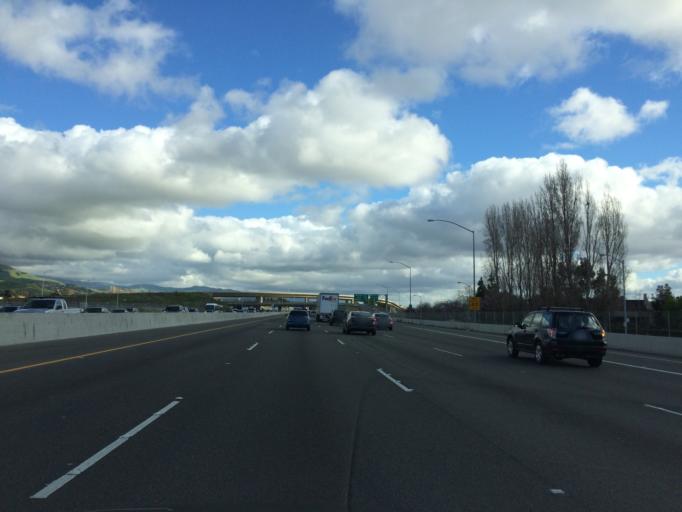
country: US
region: California
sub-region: Santa Clara County
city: Milpitas
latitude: 37.4876
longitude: -121.9421
